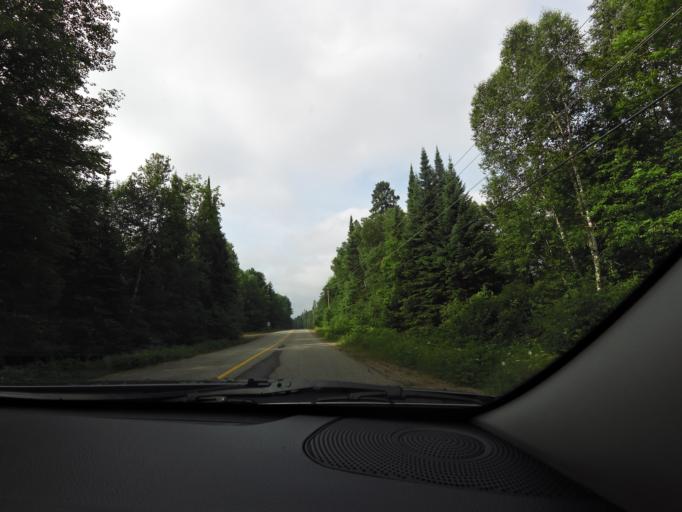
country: CA
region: Ontario
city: Huntsville
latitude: 45.6237
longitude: -79.1542
